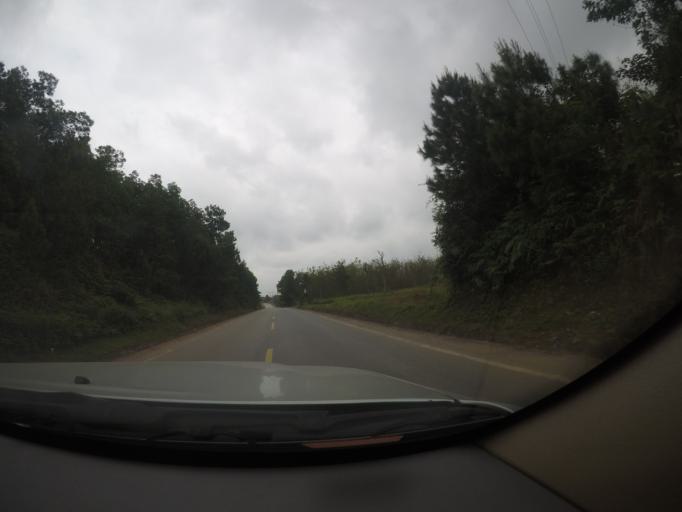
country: VN
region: Quang Binh
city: Kien Giang
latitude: 17.1549
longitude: 106.7486
